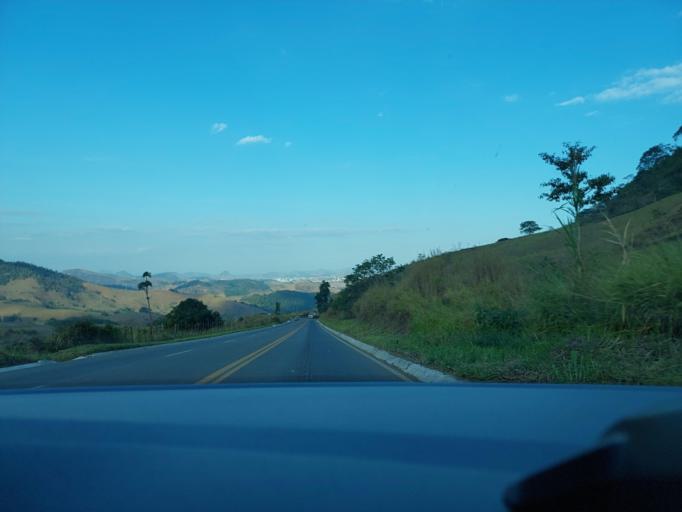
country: BR
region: Minas Gerais
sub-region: Muriae
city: Muriae
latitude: -21.0861
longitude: -42.4887
